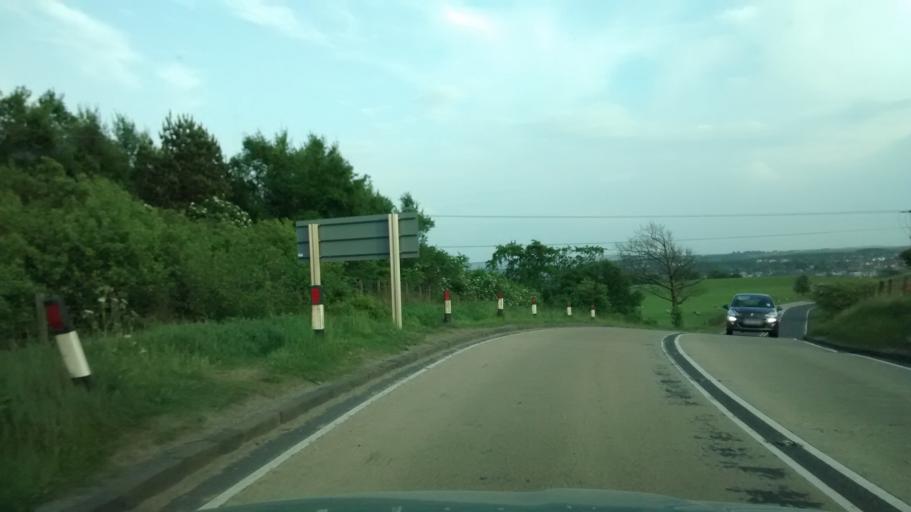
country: GB
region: Scotland
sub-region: West Lothian
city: Armadale
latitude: 55.8807
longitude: -3.6860
